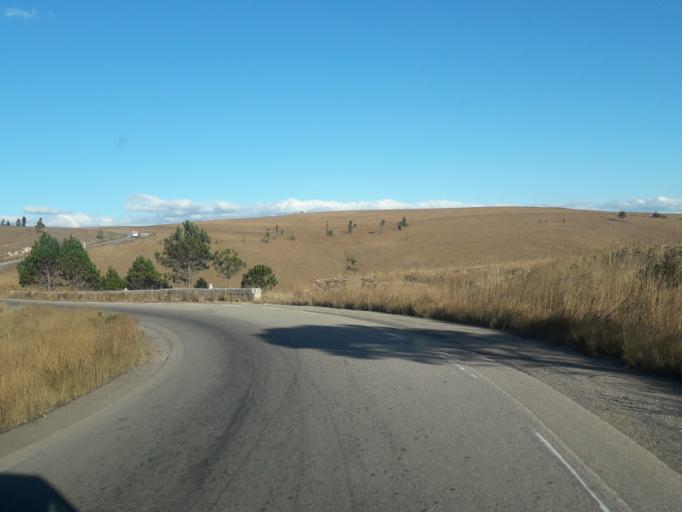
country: MG
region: Analamanga
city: Ankazobe
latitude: -18.0312
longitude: 47.1674
